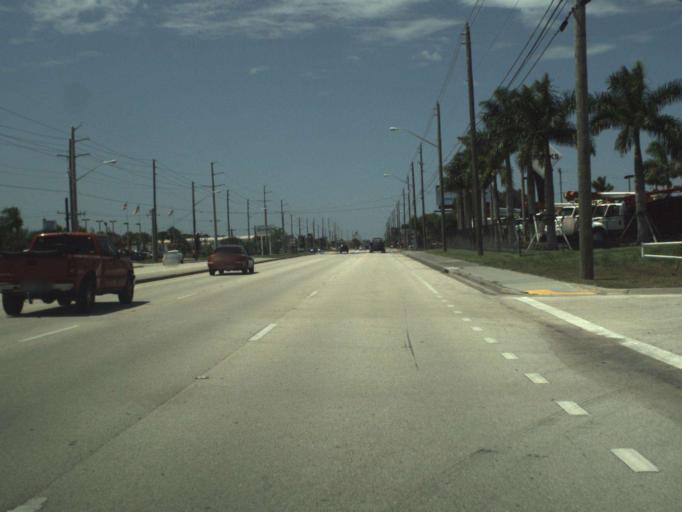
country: US
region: Florida
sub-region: Saint Lucie County
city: White City
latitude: 27.3665
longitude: -80.3257
